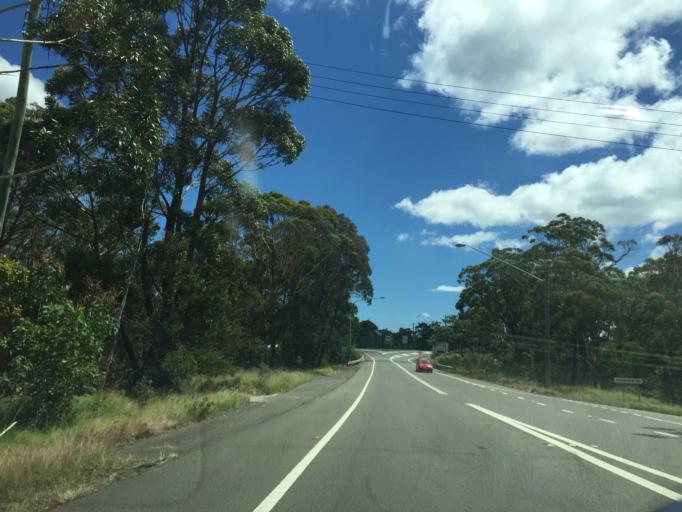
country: AU
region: New South Wales
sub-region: Blue Mountains Municipality
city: Blackheath
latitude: -33.5116
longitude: 150.2832
